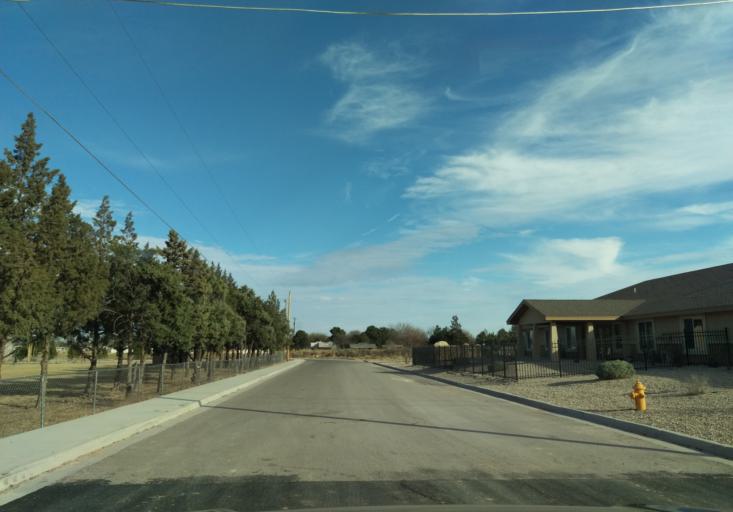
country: US
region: New Mexico
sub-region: Eddy County
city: La Huerta
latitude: 32.4491
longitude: -104.2389
